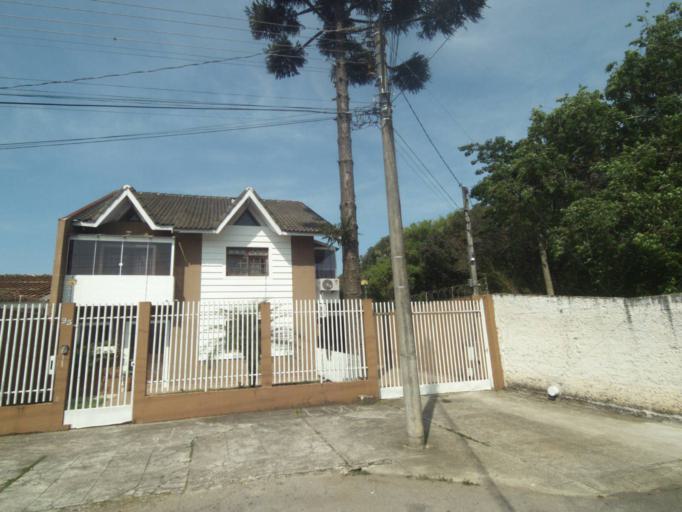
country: BR
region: Parana
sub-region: Curitiba
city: Curitiba
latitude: -25.4658
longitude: -49.3197
